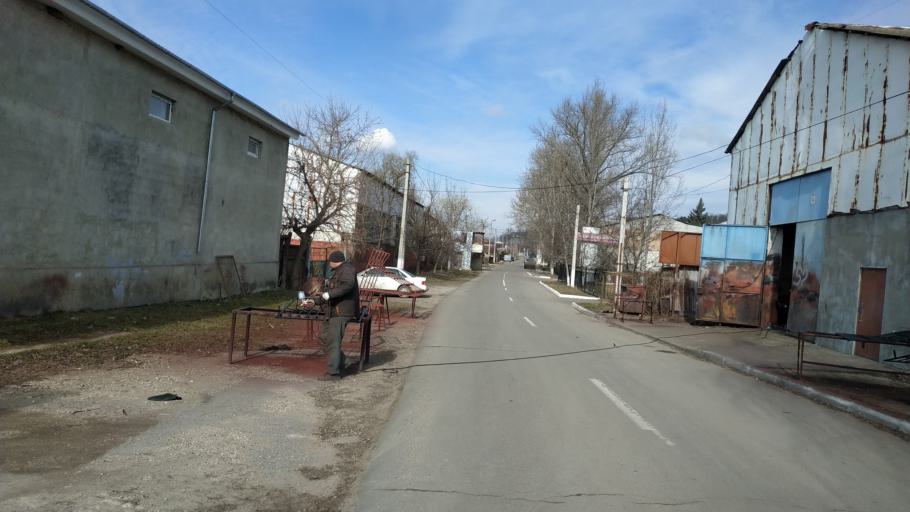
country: MD
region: Hincesti
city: Hincesti
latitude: 46.8289
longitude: 28.6057
